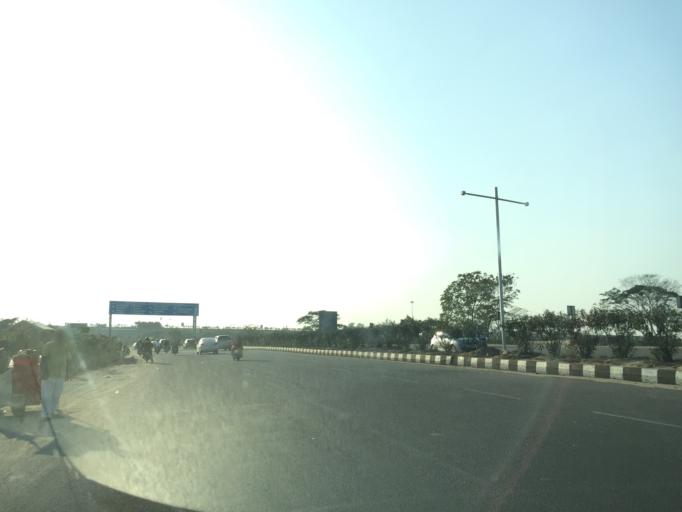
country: IN
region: Telangana
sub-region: Rangareddi
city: Ghatkesar
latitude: 17.4426
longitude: 78.6723
